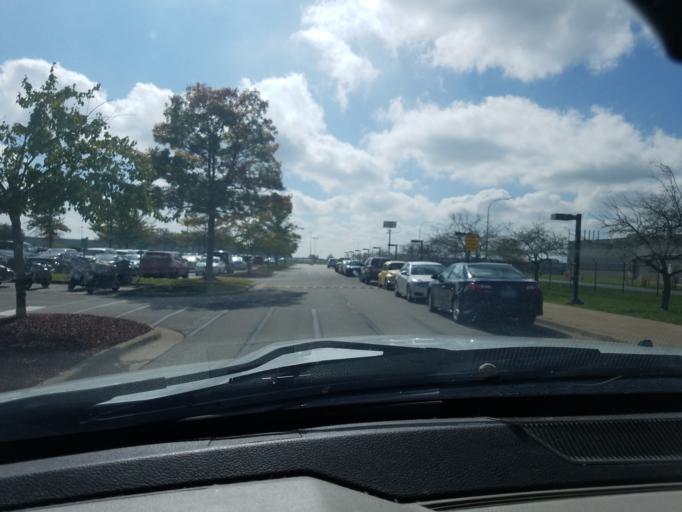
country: US
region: Kentucky
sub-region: Scott County
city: Georgetown
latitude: 38.2533
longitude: -84.5318
